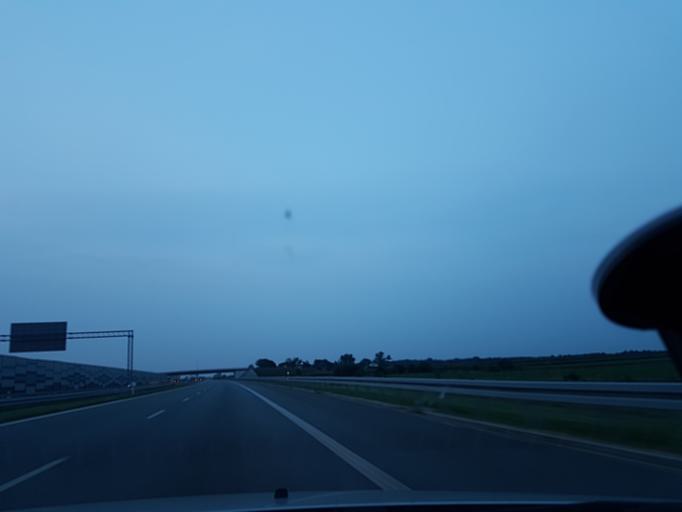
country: PL
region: Lodz Voivodeship
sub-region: Powiat leczycki
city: Piatek
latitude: 52.0510
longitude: 19.5364
